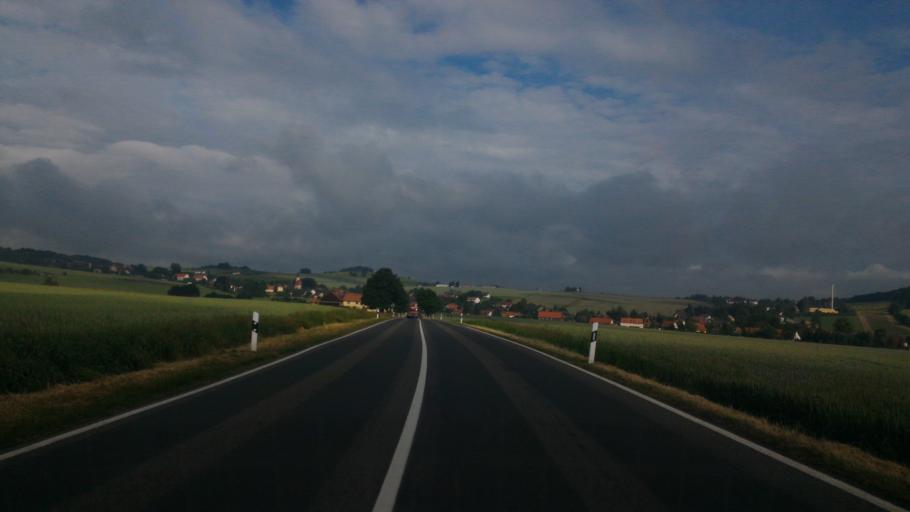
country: DE
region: Saxony
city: Hainewalde
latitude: 50.9348
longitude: 14.6982
